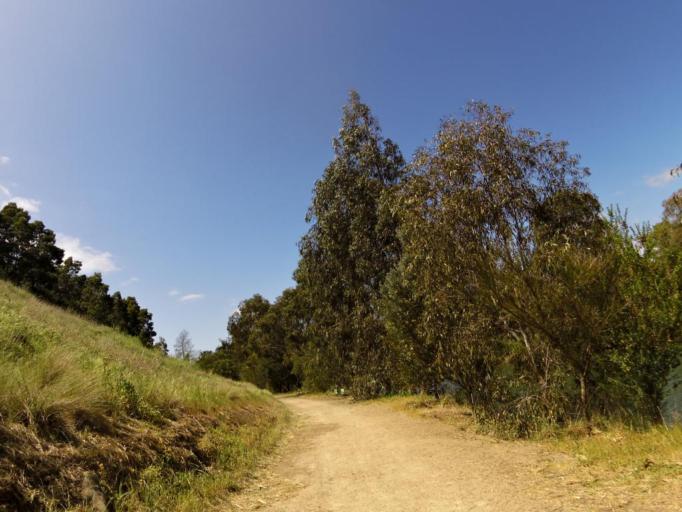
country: AU
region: Victoria
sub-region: Moonee Valley
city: Essendon West
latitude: -37.7610
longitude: 144.8739
